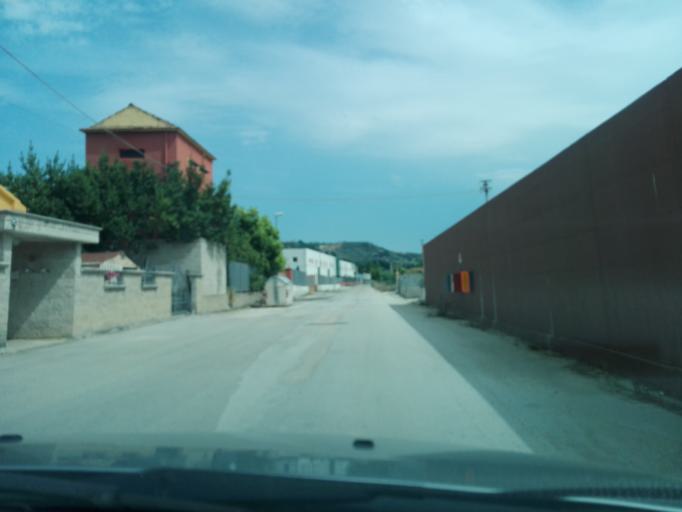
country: IT
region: Abruzzo
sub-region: Provincia di Pescara
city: Cappelle sul Tavo
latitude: 42.4863
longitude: 14.1117
